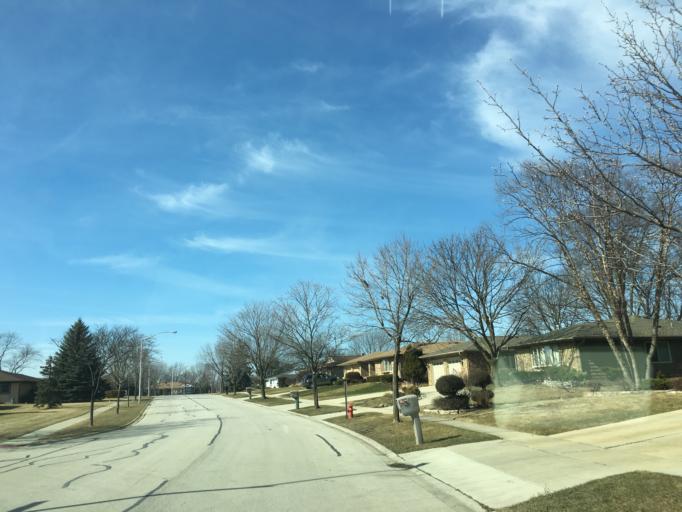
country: US
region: Illinois
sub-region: DuPage County
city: Hanover Park
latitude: 42.0237
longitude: -88.1298
